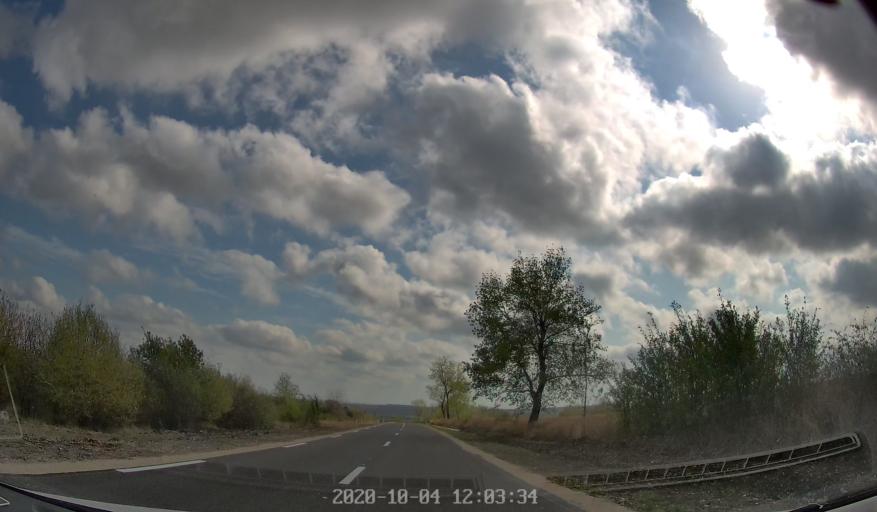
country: MD
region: Rezina
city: Saharna
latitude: 47.6110
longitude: 28.9294
